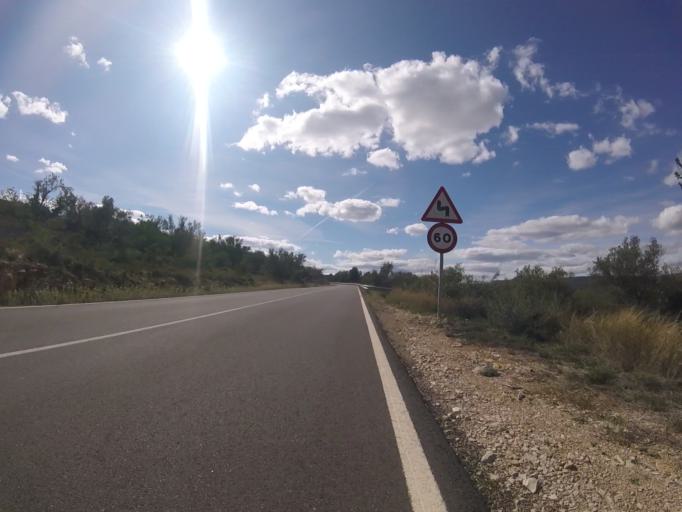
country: ES
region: Valencia
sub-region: Provincia de Castello
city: Cati
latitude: 40.4306
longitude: 0.0934
